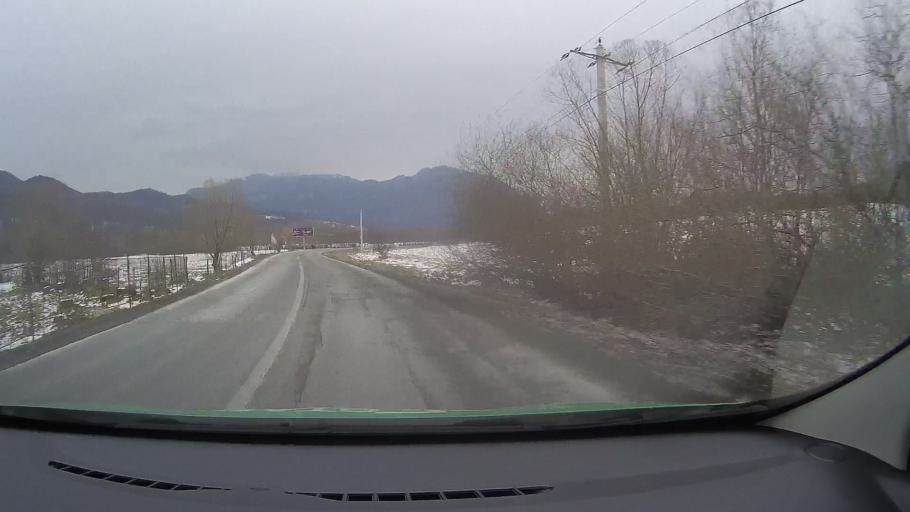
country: RO
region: Brasov
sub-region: Oras Rasnov
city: Rasnov
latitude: 45.5559
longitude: 25.4755
